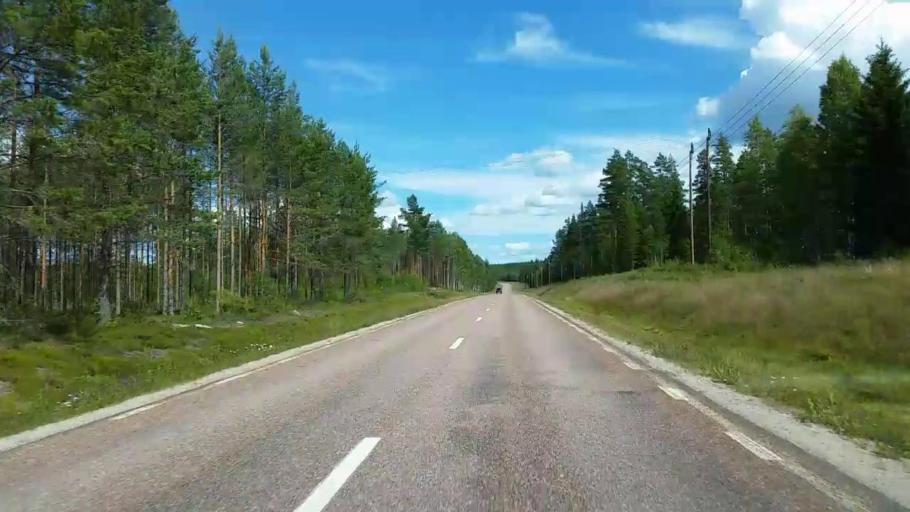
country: SE
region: Dalarna
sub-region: Rattviks Kommun
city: Raettvik
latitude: 61.1939
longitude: 15.3281
